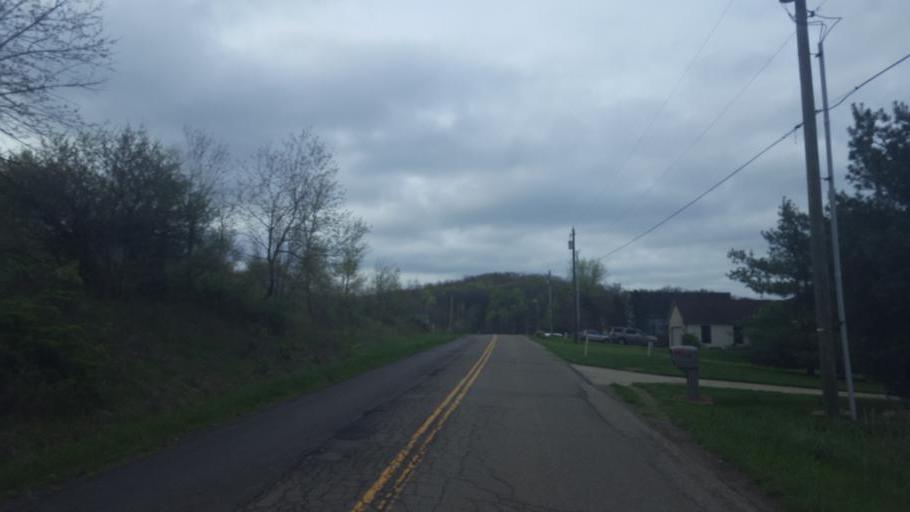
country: US
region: Ohio
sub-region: Knox County
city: Danville
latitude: 40.4615
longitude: -82.3360
